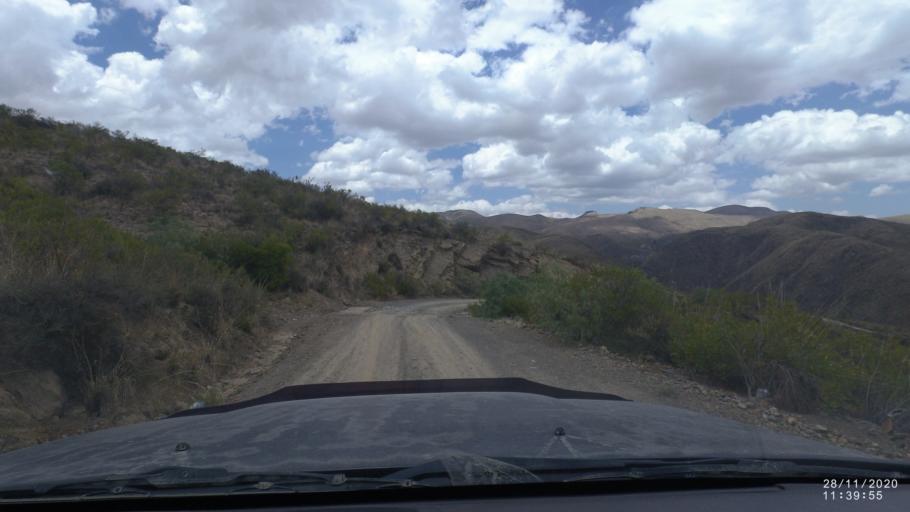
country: BO
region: Cochabamba
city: Tarata
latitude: -17.6747
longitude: -66.0446
